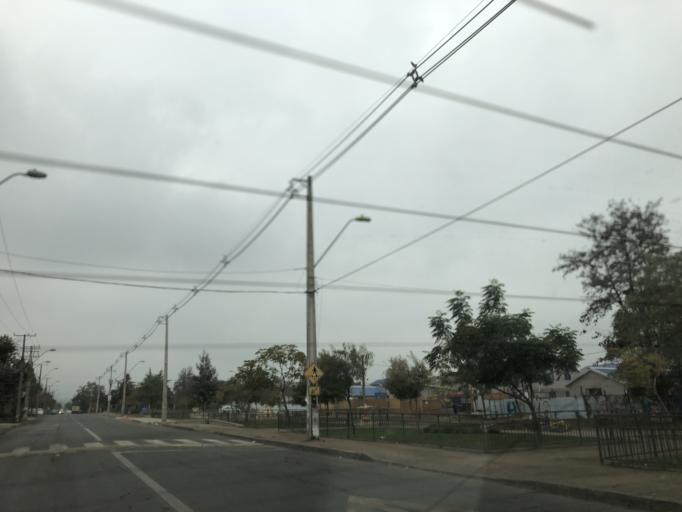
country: CL
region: Santiago Metropolitan
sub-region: Provincia de Santiago
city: La Pintana
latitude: -33.5851
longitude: -70.6080
